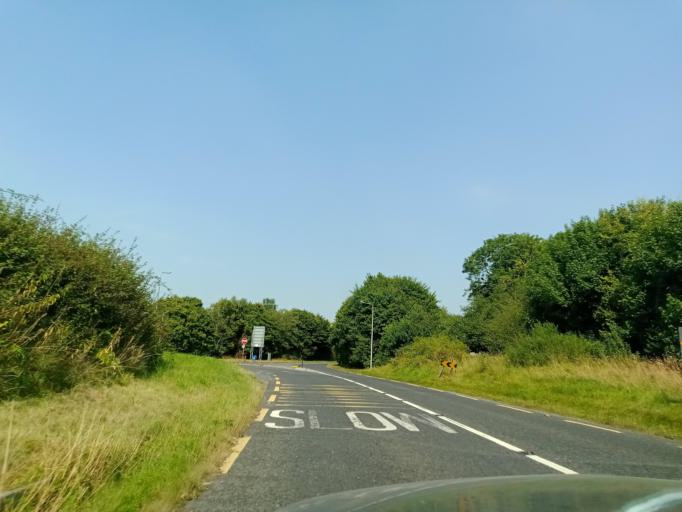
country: IE
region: Leinster
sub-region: Laois
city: Portlaoise
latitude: 53.0463
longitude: -7.2465
